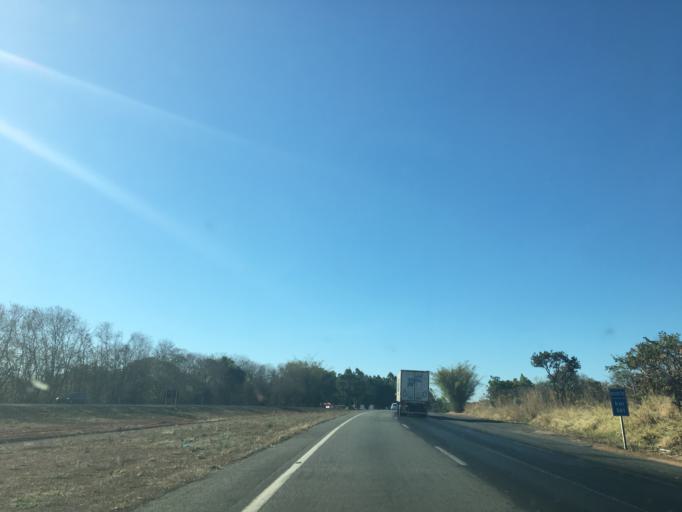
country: BR
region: Goias
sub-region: Hidrolandia
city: Hidrolandia
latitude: -17.0554
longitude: -49.2265
